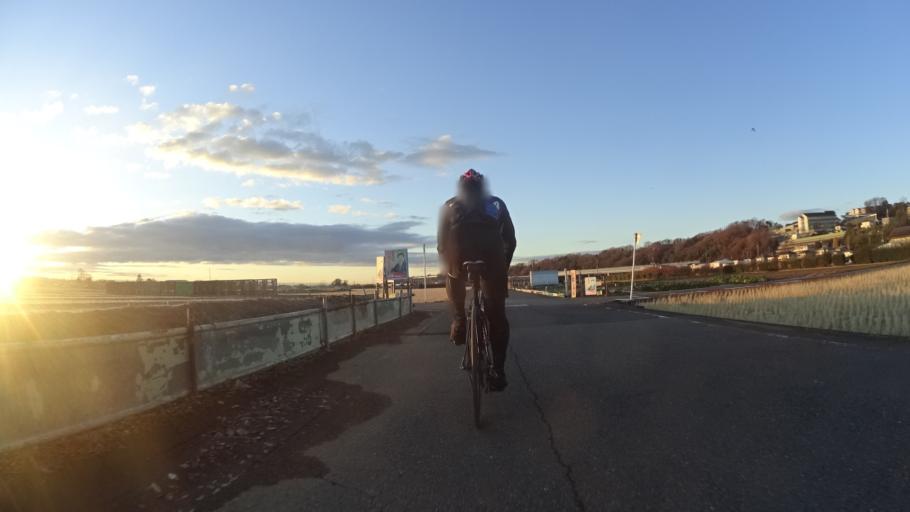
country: JP
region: Kanagawa
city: Zama
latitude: 35.5134
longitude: 139.3682
